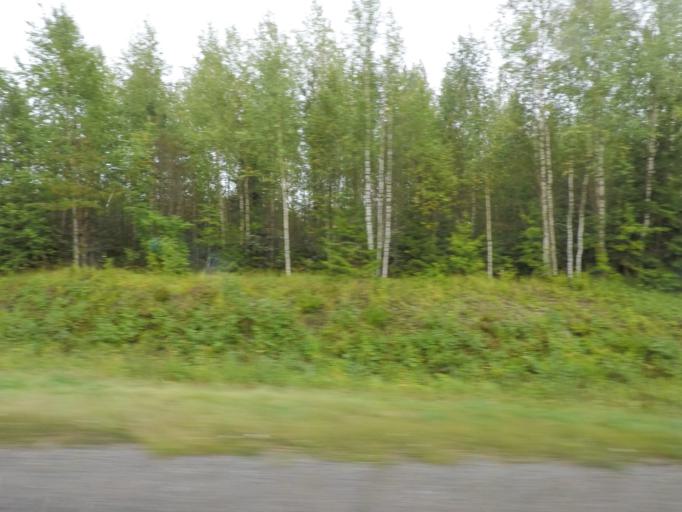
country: FI
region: Southern Savonia
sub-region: Pieksaemaeki
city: Juva
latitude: 62.0064
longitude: 27.8020
